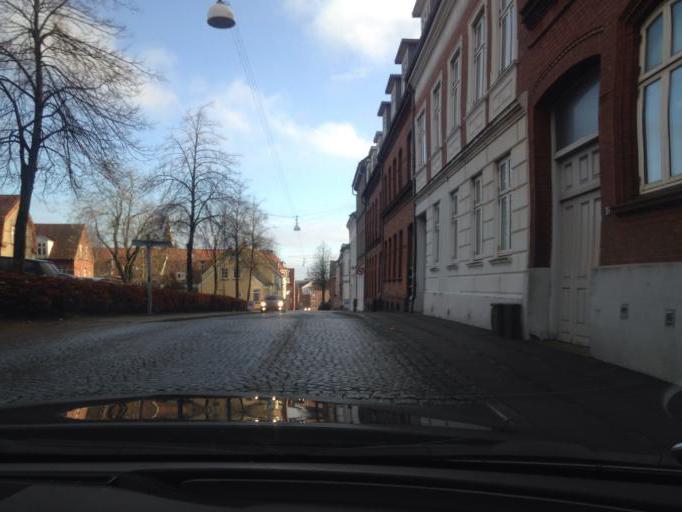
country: DK
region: South Denmark
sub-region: Kolding Kommune
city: Kolding
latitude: 55.4913
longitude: 9.4666
